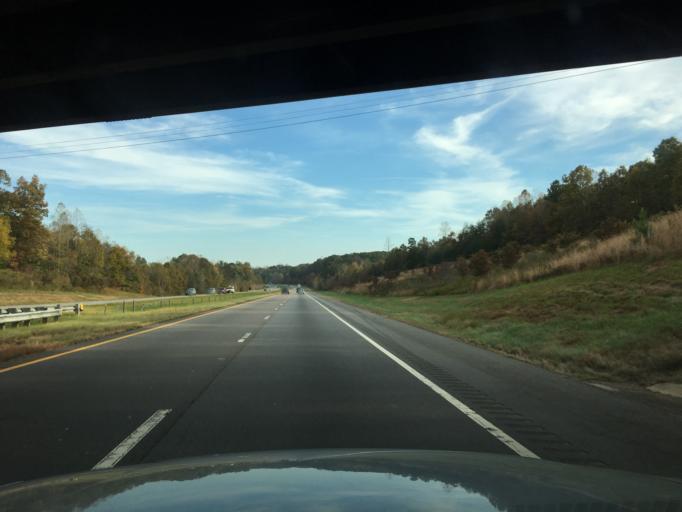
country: US
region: North Carolina
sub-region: Catawba County
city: Mountain View
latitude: 35.6571
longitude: -81.3182
